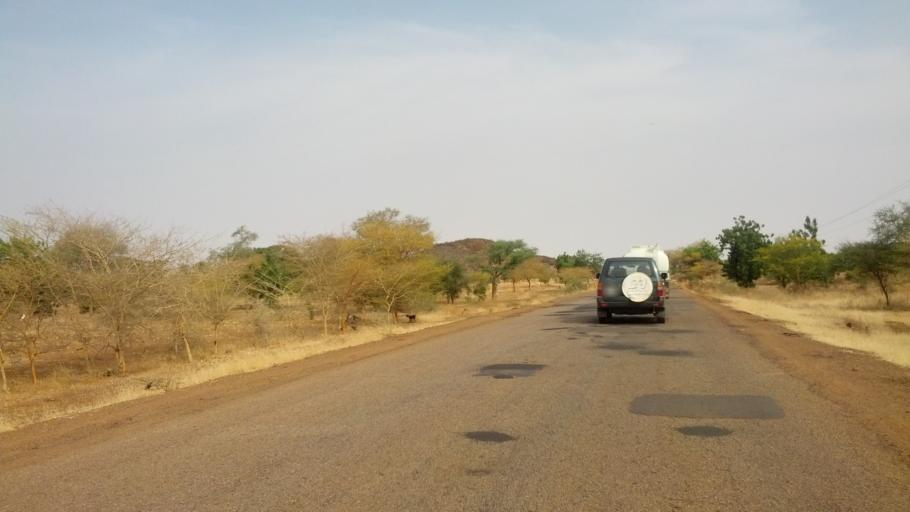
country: BF
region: Centre-Nord
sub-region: Province du Sanmatenga
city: Kaya
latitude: 12.9207
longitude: -1.0778
